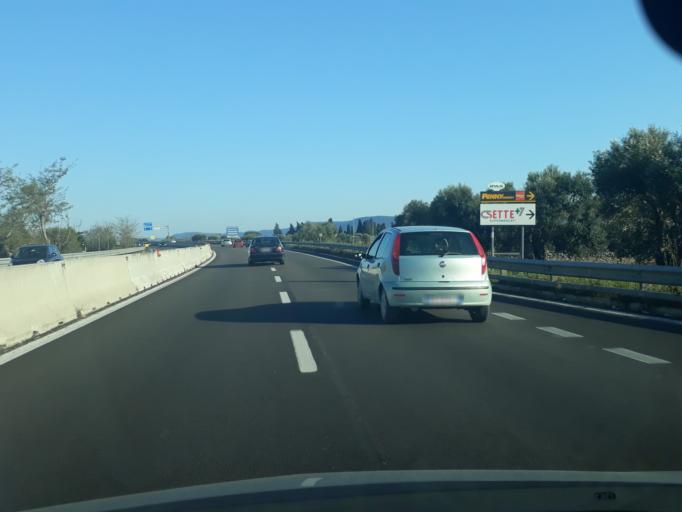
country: IT
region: Apulia
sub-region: Provincia di Brindisi
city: Fasano
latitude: 40.8438
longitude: 17.3649
